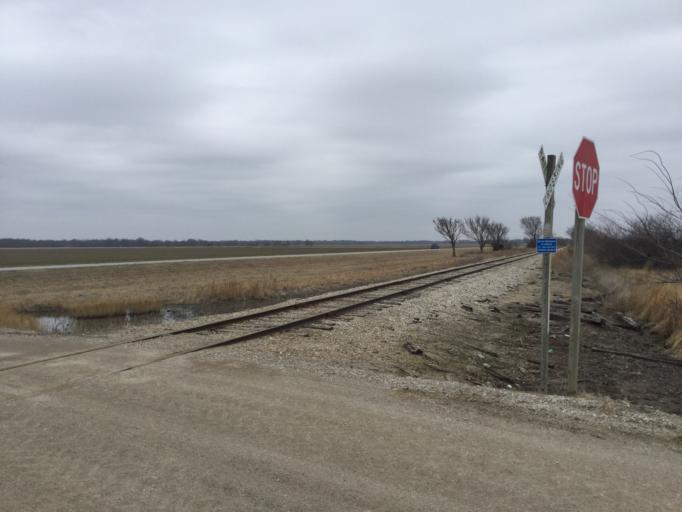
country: US
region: Kansas
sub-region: Labette County
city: Oswego
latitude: 37.1664
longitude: -95.0319
